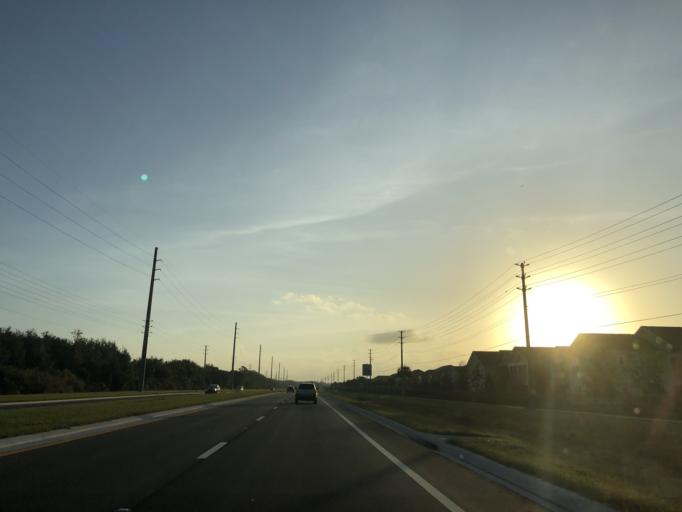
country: US
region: Florida
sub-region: Osceola County
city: Kissimmee
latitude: 28.3252
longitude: -81.4355
